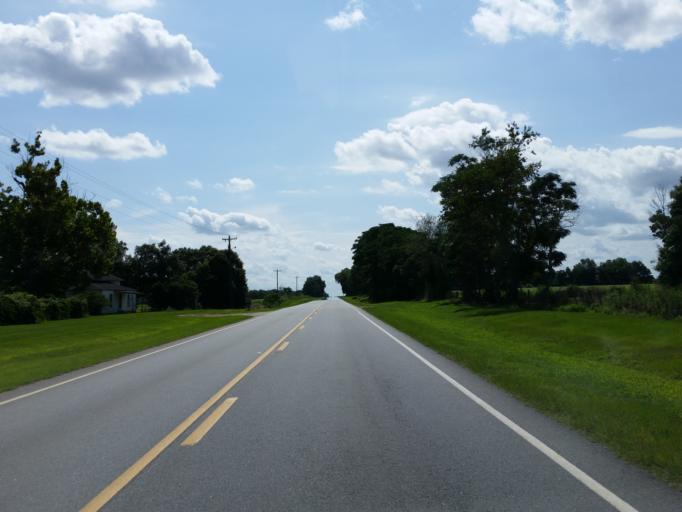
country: US
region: Georgia
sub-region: Turner County
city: Ashburn
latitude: 31.6359
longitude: -83.4801
